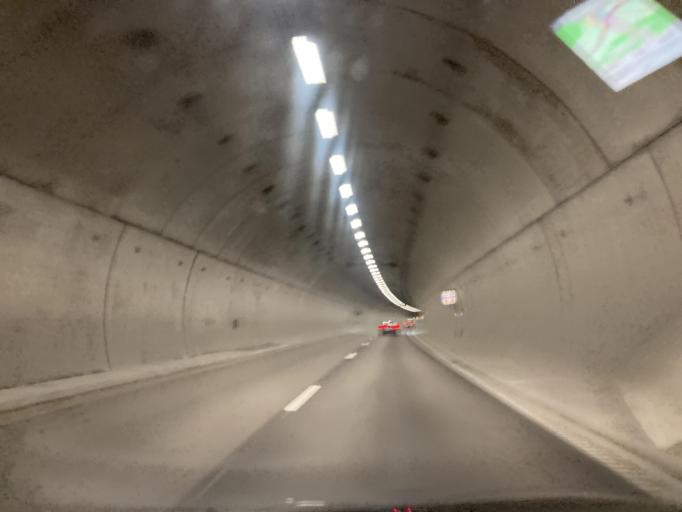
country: NO
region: Akershus
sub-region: Eidsvoll
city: Eidsvoll
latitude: 60.3425
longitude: 11.2045
